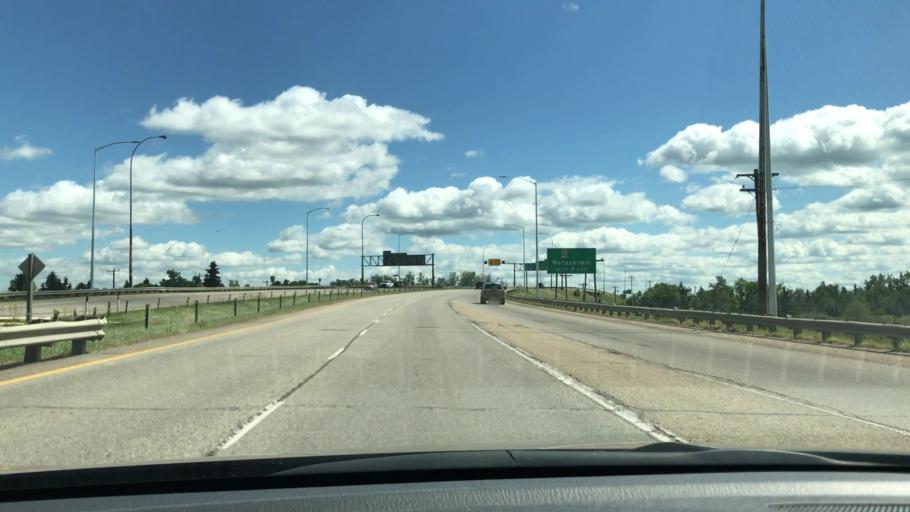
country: CA
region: Alberta
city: Leduc
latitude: 53.2611
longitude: -113.5627
